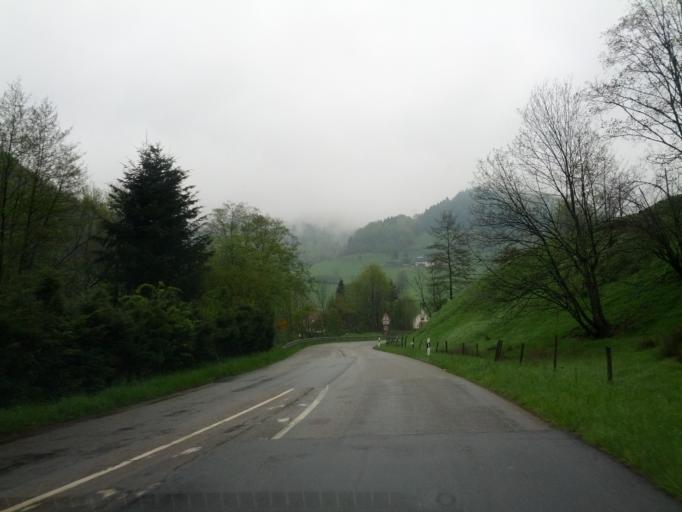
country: DE
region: Baden-Wuerttemberg
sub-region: Freiburg Region
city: Muenstertal/Schwarzwald
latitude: 47.8769
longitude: 7.8350
